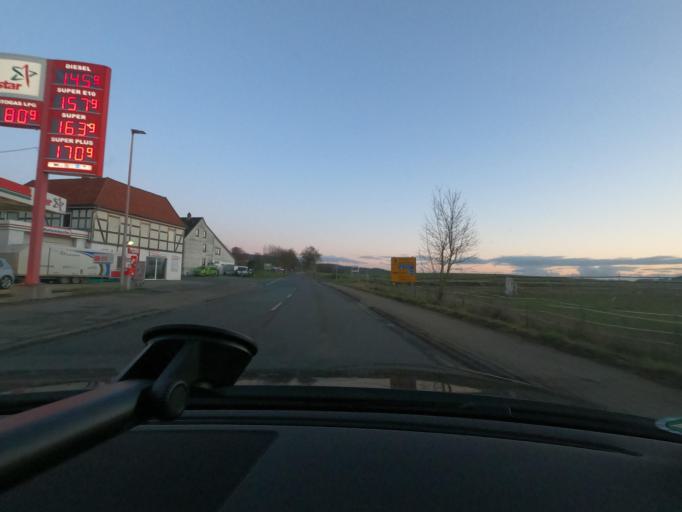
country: DE
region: Lower Saxony
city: Badenhausen
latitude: 51.7817
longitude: 10.1994
